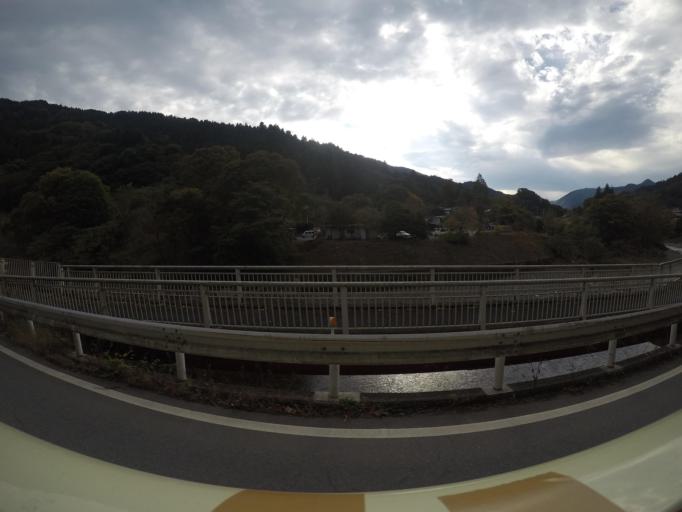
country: JP
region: Gunma
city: Tomioka
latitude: 36.1163
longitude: 138.9323
